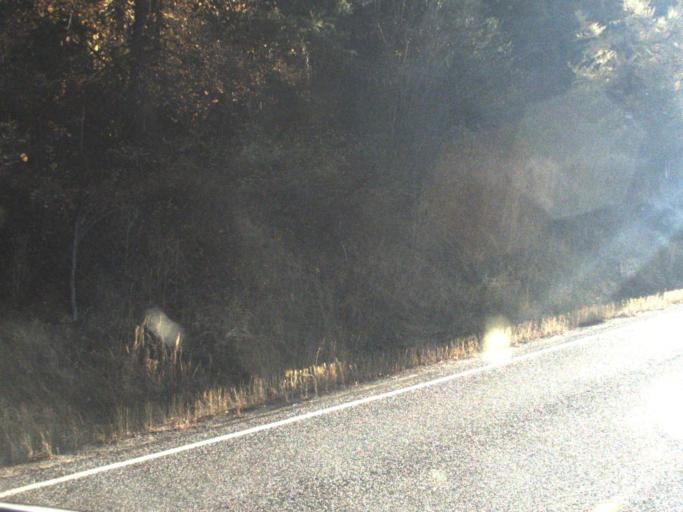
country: CA
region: British Columbia
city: Rossland
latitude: 48.8700
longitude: -117.8623
